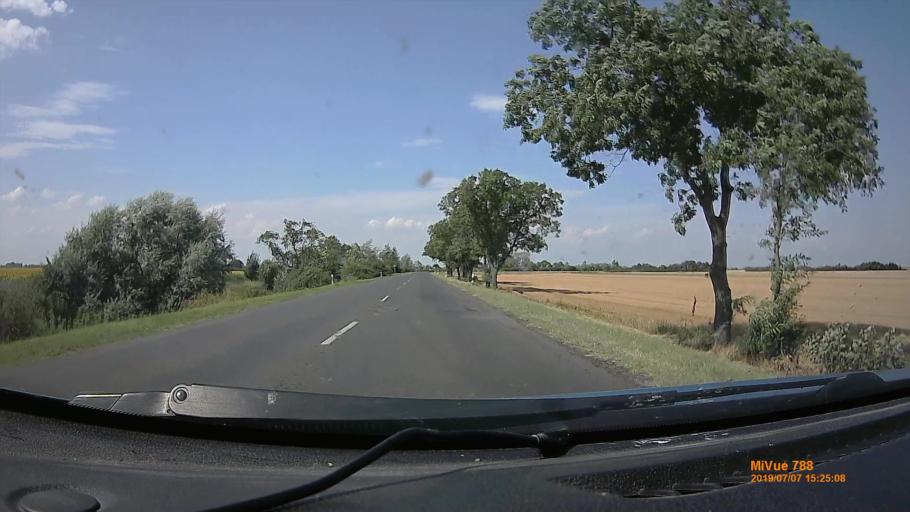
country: HU
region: Jasz-Nagykun-Szolnok
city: Janoshida
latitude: 47.4018
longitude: 20.0592
